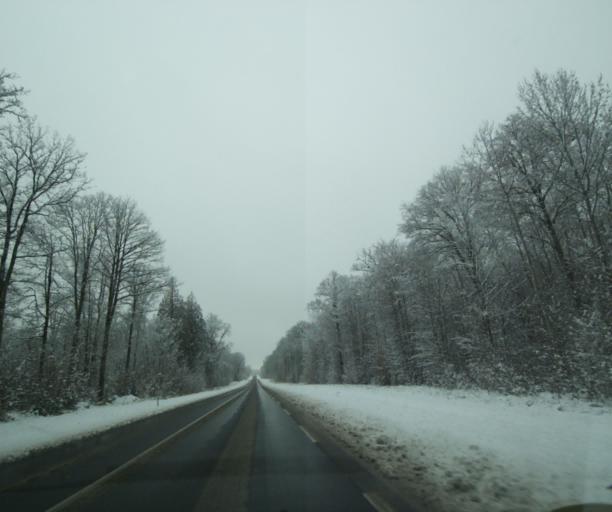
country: FR
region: Champagne-Ardenne
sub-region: Departement de la Haute-Marne
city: Laneuville-a-Remy
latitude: 48.5565
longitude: 4.8392
